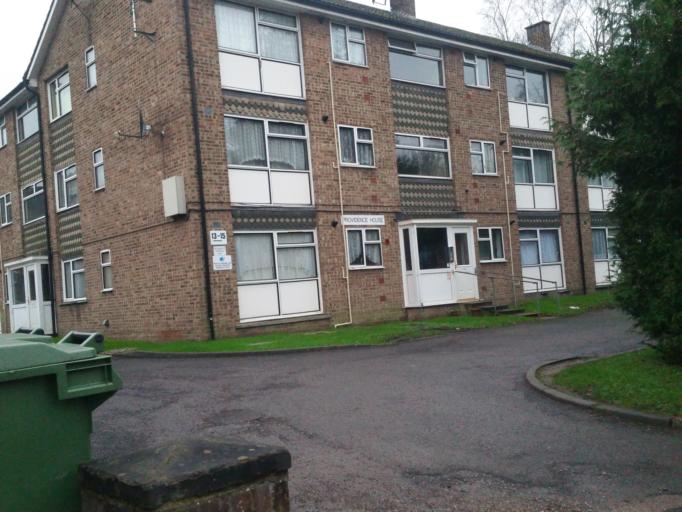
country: GB
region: England
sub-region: Surrey
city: Bagshot
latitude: 51.3612
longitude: -0.6888
